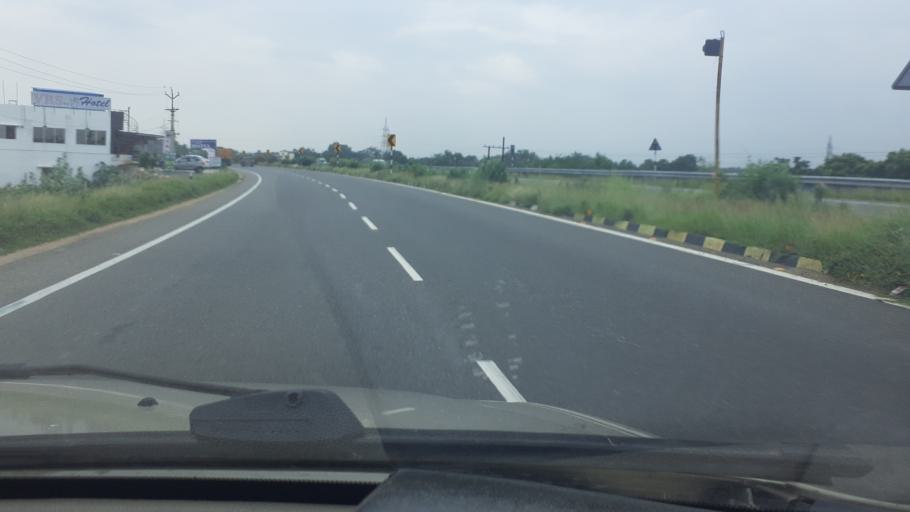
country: IN
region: Tamil Nadu
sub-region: Madurai
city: Tirupparangunram
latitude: 9.8335
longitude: 77.9769
